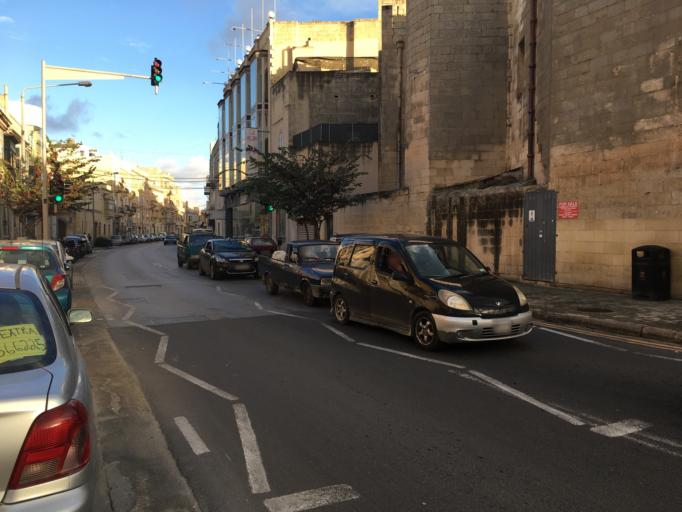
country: MT
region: Birkirkara
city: Birkirkara
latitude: 35.8954
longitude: 14.4656
